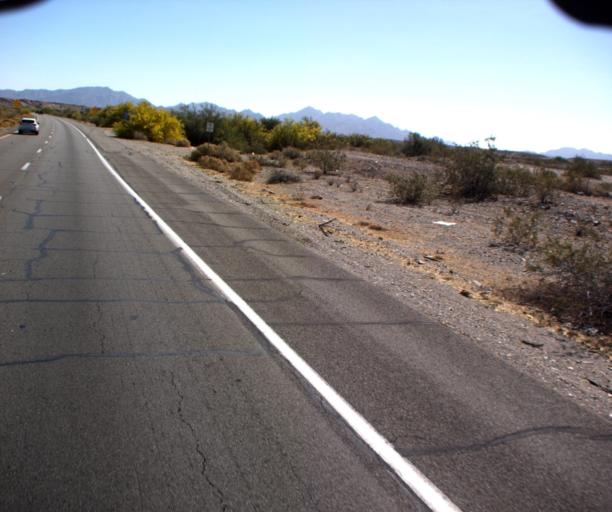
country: US
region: Arizona
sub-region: La Paz County
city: Ehrenberg
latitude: 33.6026
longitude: -114.5113
